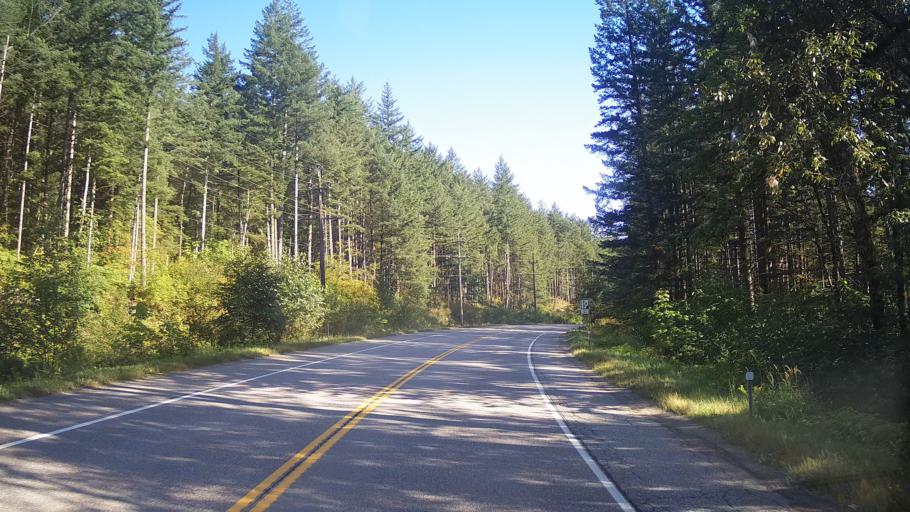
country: CA
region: British Columbia
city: Hope
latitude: 49.4332
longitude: -121.4393
